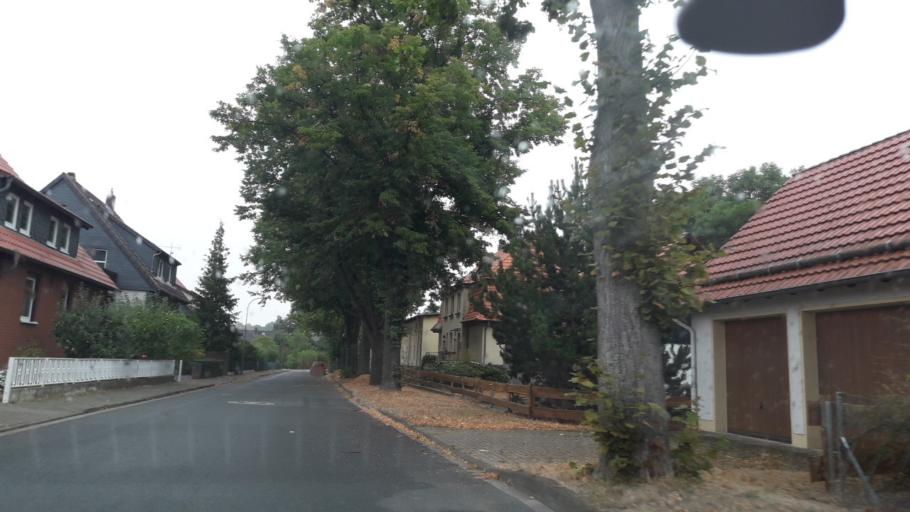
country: DE
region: Lower Saxony
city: Vienenburg
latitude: 51.9617
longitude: 10.5907
